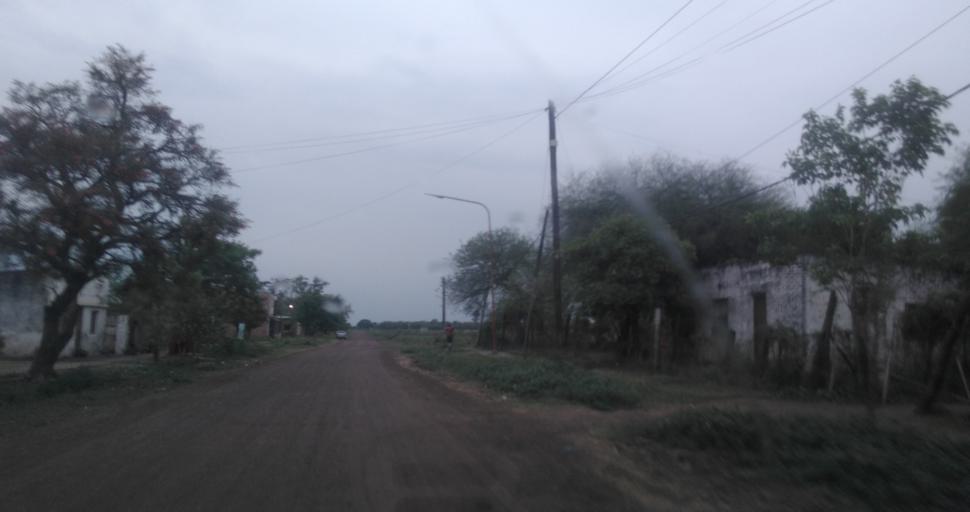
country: AR
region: Chaco
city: Fontana
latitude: -27.4203
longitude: -59.0398
